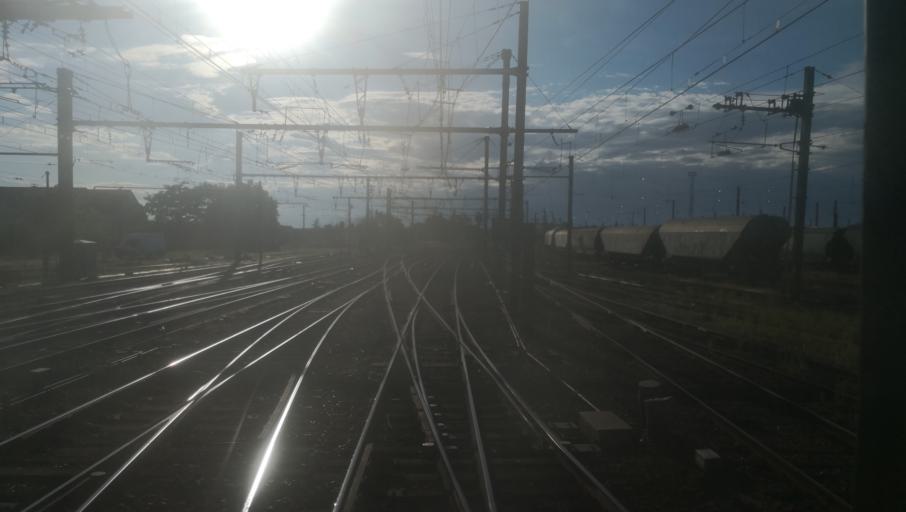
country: FR
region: Centre
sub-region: Departement du Cher
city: Vierzon
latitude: 47.2278
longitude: 2.0558
